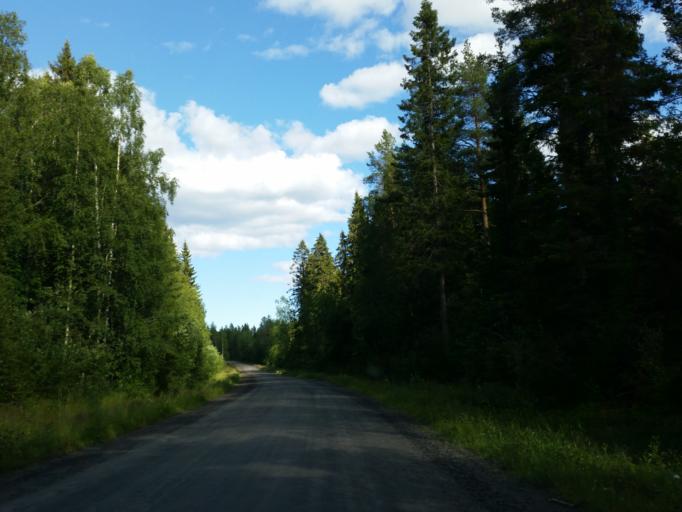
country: SE
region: Vaesterbotten
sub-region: Robertsfors Kommun
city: Robertsfors
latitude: 64.1391
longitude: 20.8675
